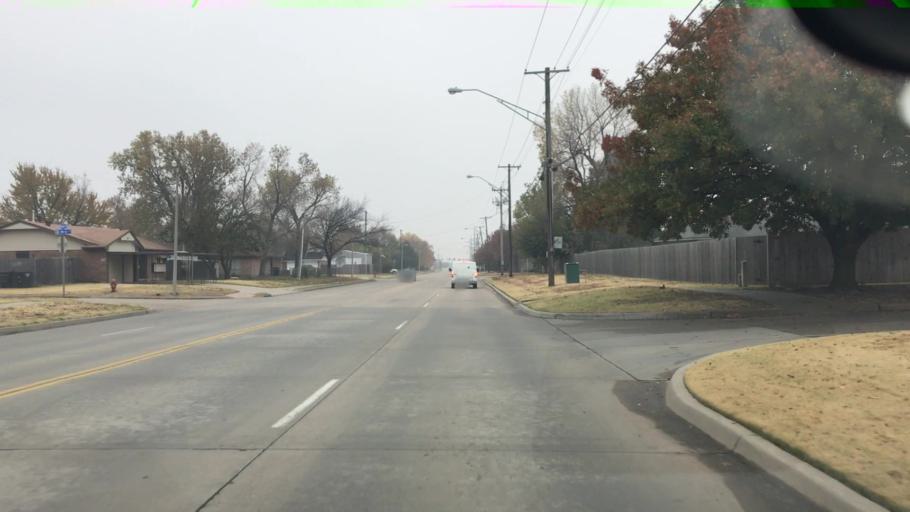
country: US
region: Oklahoma
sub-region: Cleveland County
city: Moore
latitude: 35.3394
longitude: -97.5122
